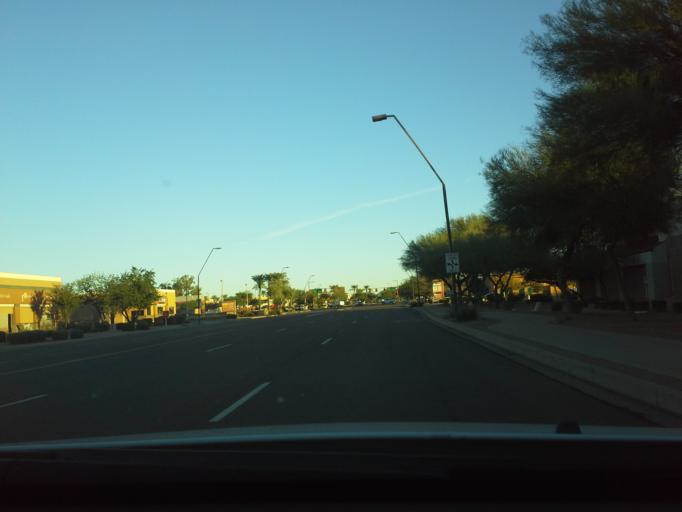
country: US
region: Arizona
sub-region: Maricopa County
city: Guadalupe
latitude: 33.3469
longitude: -111.9631
